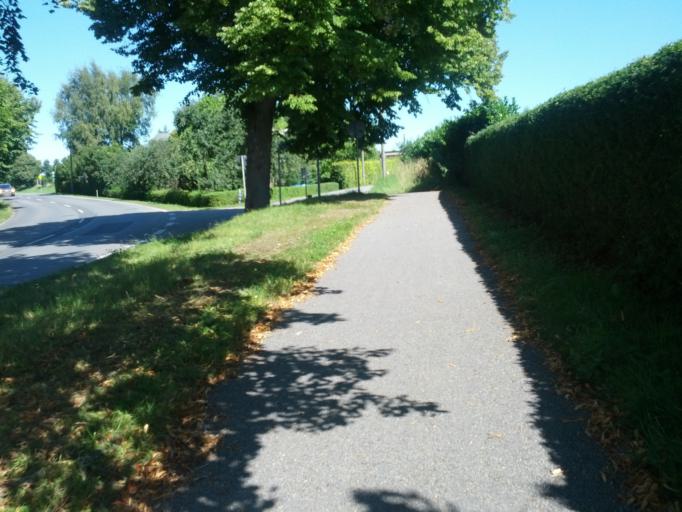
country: DE
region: Mecklenburg-Vorpommern
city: Bastorf
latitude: 54.1263
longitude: 11.7018
